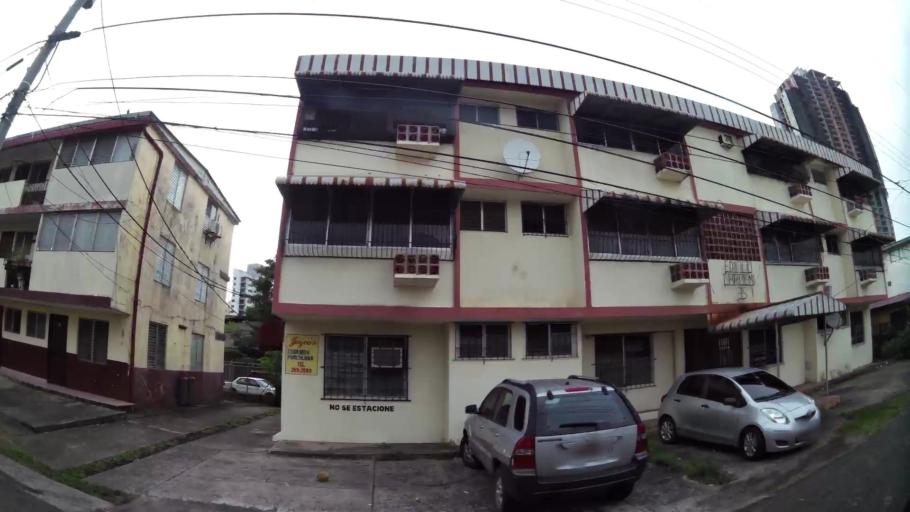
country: PA
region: Panama
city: Panama
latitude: 8.9949
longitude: -79.5179
